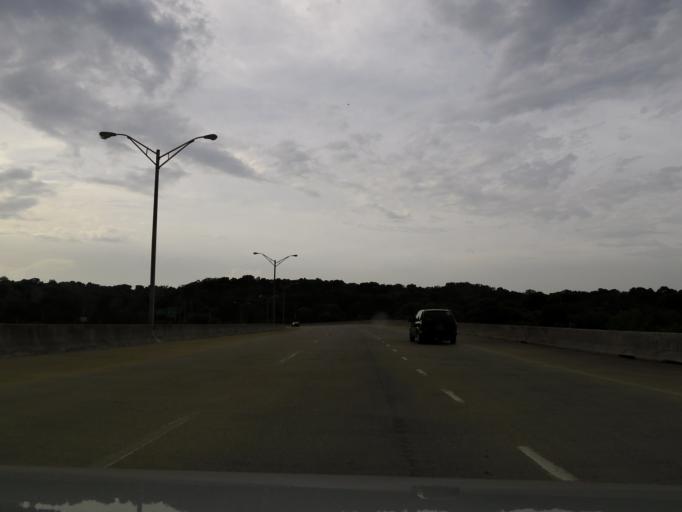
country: US
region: Tennessee
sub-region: Knox County
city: Knoxville
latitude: 35.9622
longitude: -83.8974
